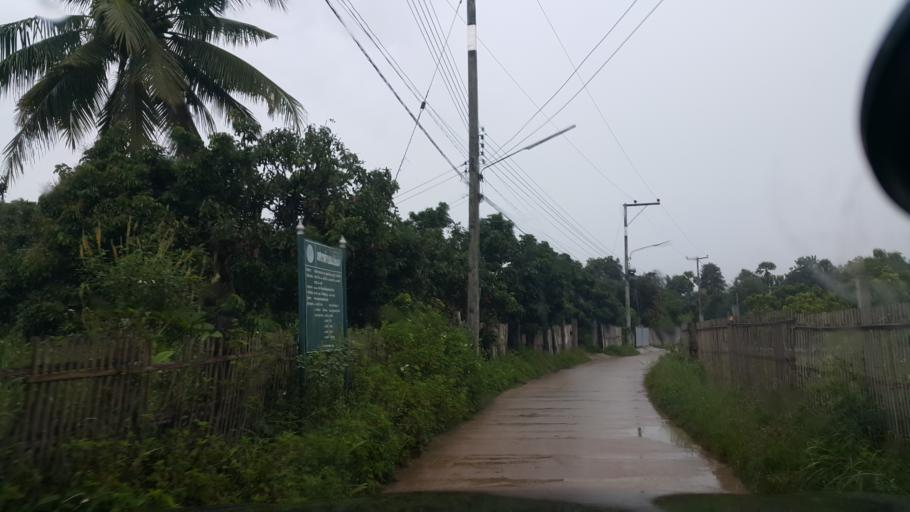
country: TH
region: Lamphun
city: Ban Thi
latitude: 18.6175
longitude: 99.1163
